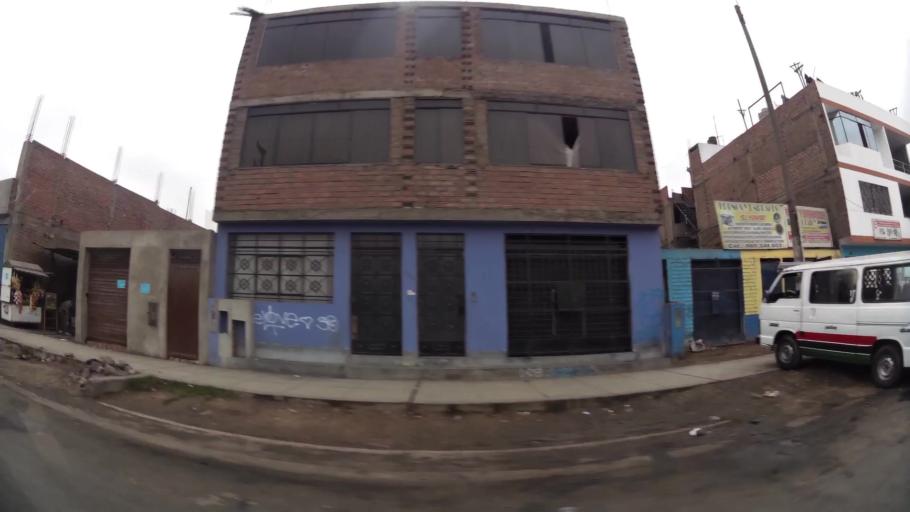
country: PE
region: Lima
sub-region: Lima
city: Vitarte
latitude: -12.0353
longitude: -76.9635
